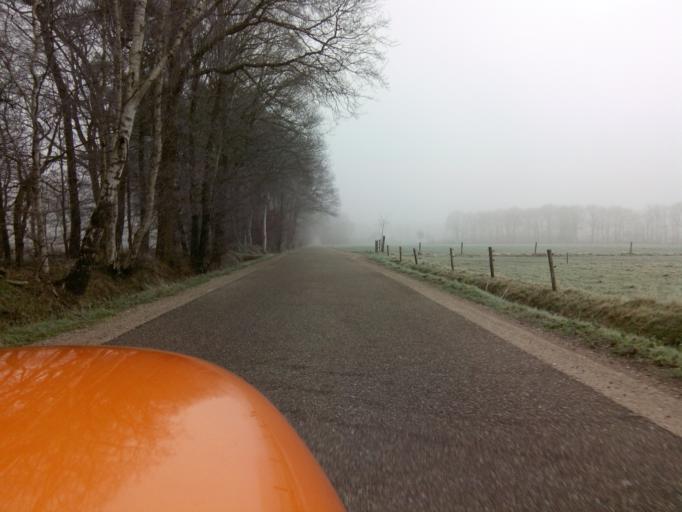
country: NL
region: Gelderland
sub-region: Gemeente Barneveld
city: Voorthuizen
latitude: 52.2003
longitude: 5.5862
